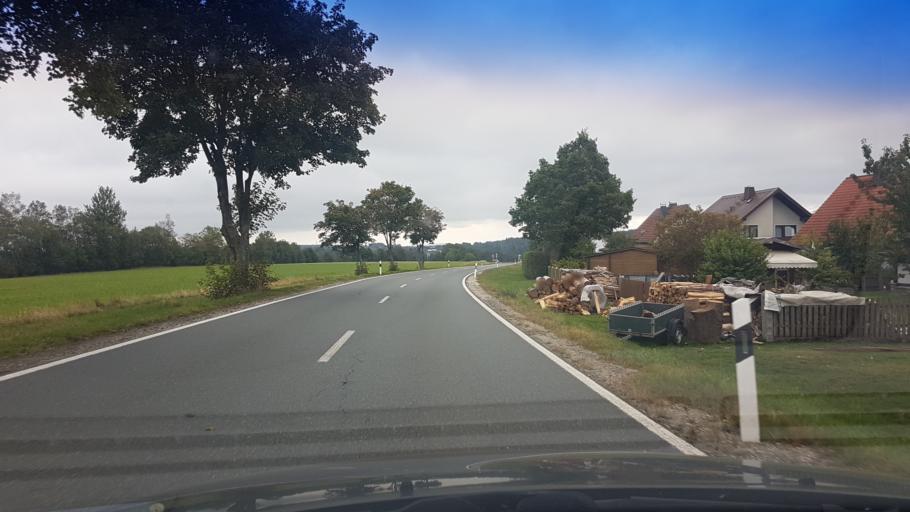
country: DE
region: Bavaria
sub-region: Upper Franconia
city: Weissenstadt
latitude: 50.0960
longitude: 11.8474
